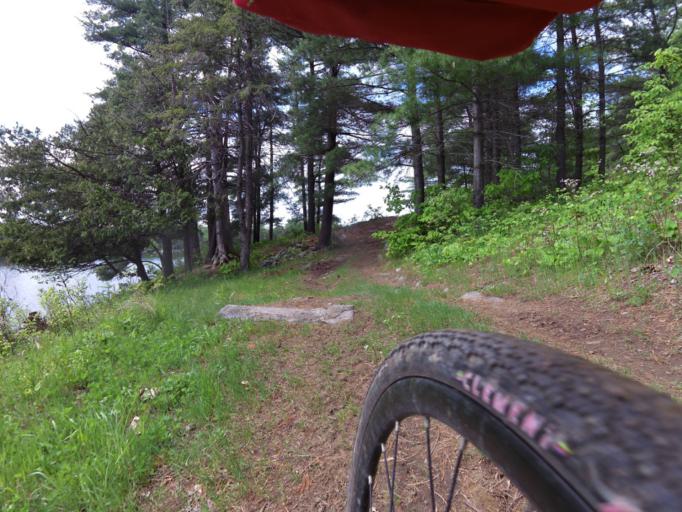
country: CA
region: Ontario
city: Renfrew
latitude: 45.1877
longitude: -76.6871
